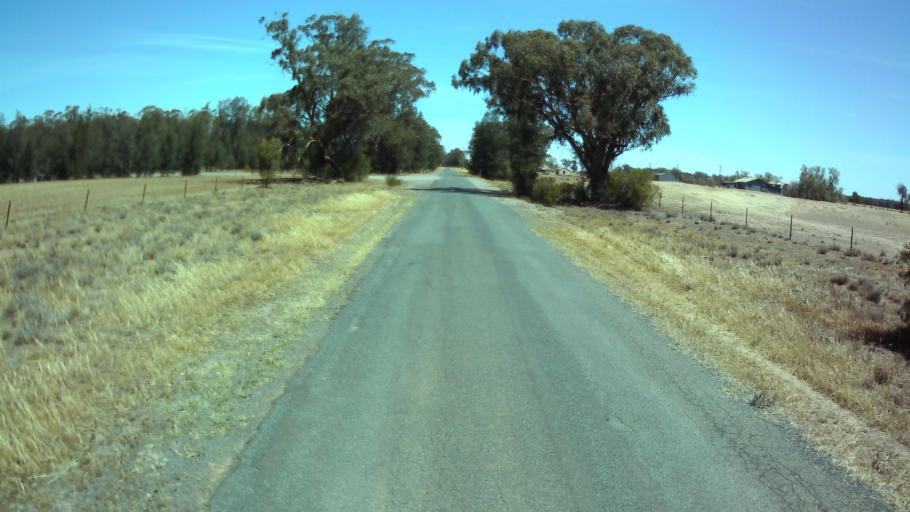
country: AU
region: New South Wales
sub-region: Weddin
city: Grenfell
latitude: -33.9024
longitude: 147.6861
